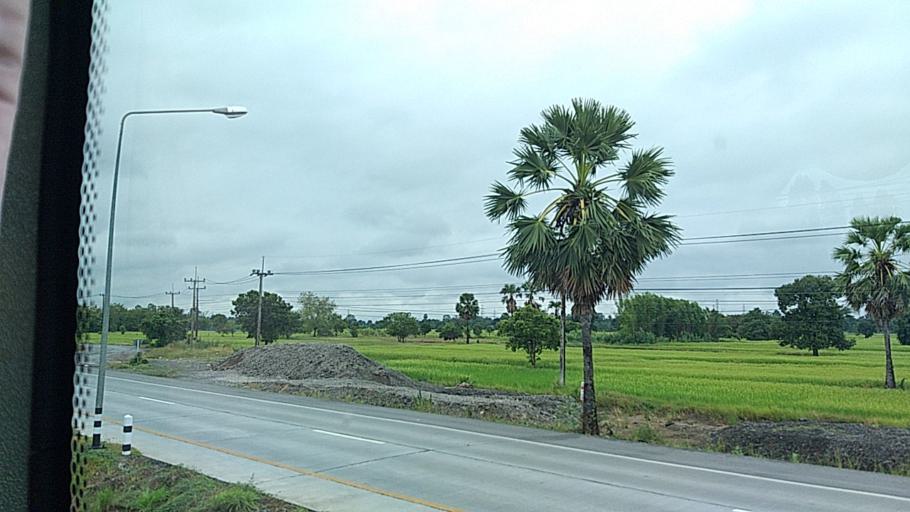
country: TH
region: Nakhon Ratchasima
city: Sida
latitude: 15.5754
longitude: 102.5550
